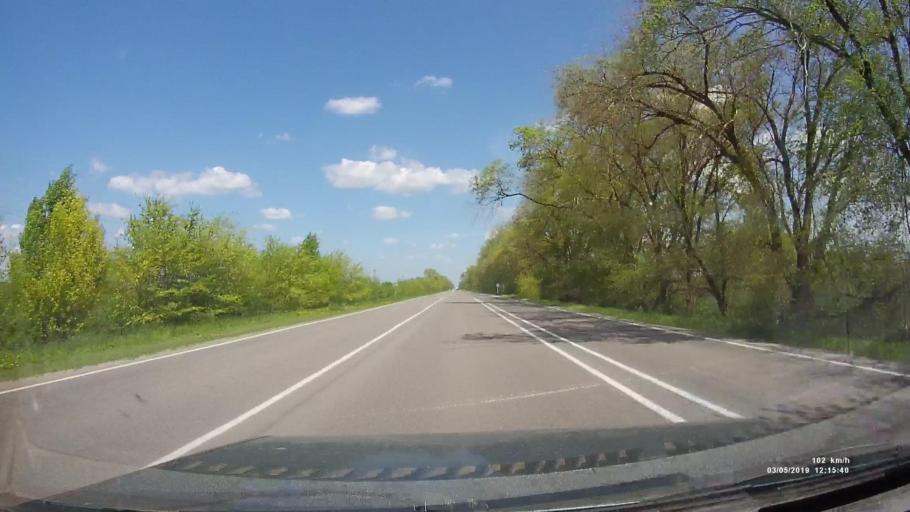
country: RU
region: Rostov
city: Melikhovskaya
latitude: 47.3610
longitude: 40.5760
